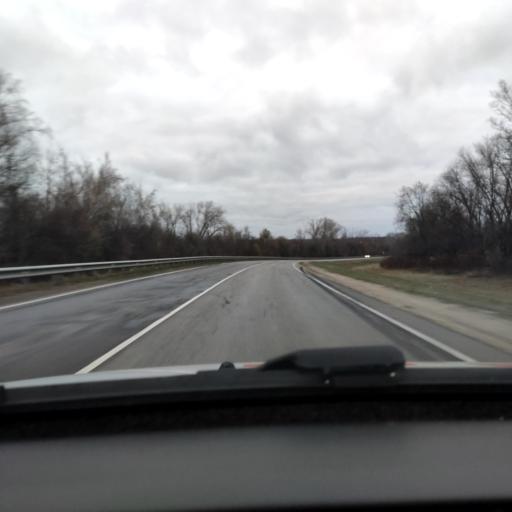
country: RU
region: Lipetsk
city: Khlevnoye
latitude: 52.3171
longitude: 39.1663
